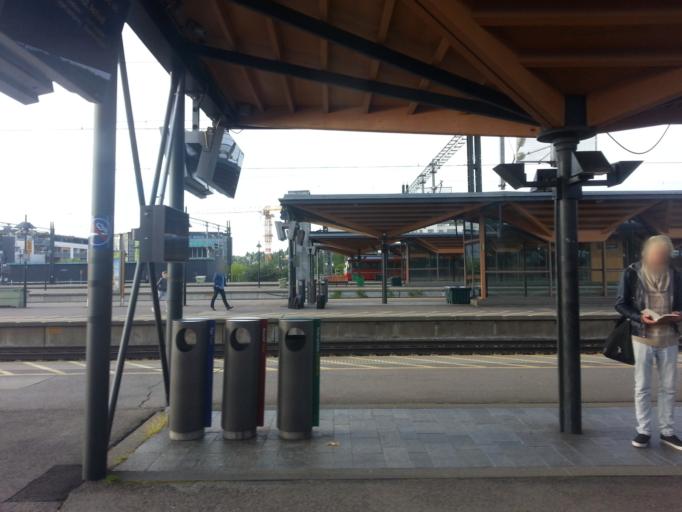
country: NO
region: Akershus
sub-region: Skedsmo
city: Lillestrom
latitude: 59.9537
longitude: 11.0454
